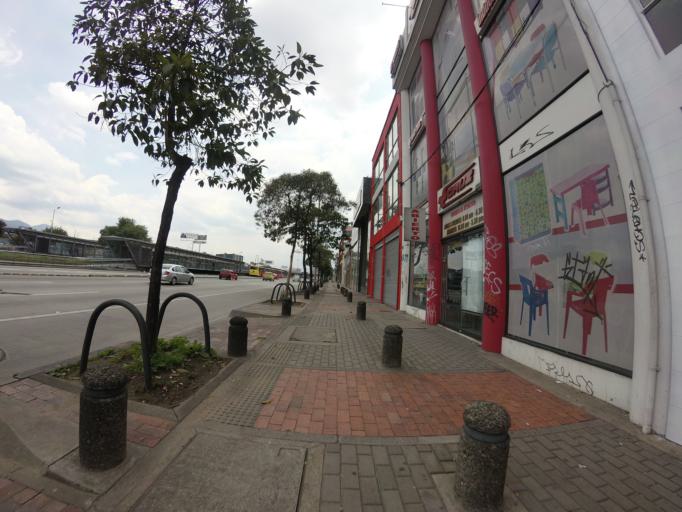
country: CO
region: Bogota D.C.
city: Barrio San Luis
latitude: 4.6701
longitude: -74.0718
